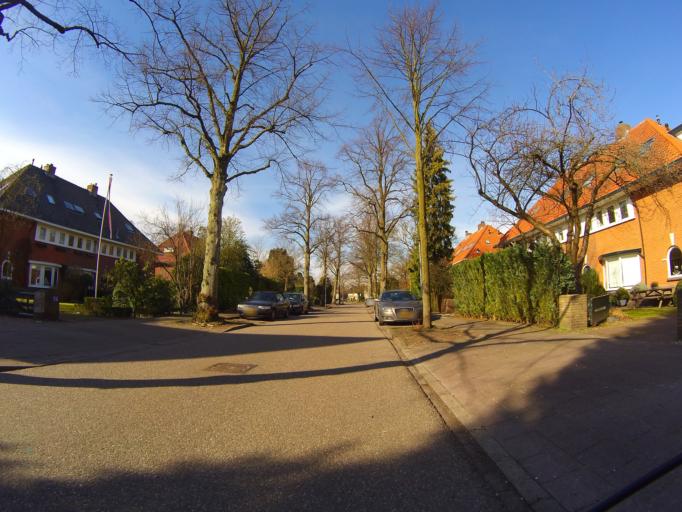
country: NL
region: North Holland
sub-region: Gemeente Naarden
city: Naarden
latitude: 52.2861
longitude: 5.1551
